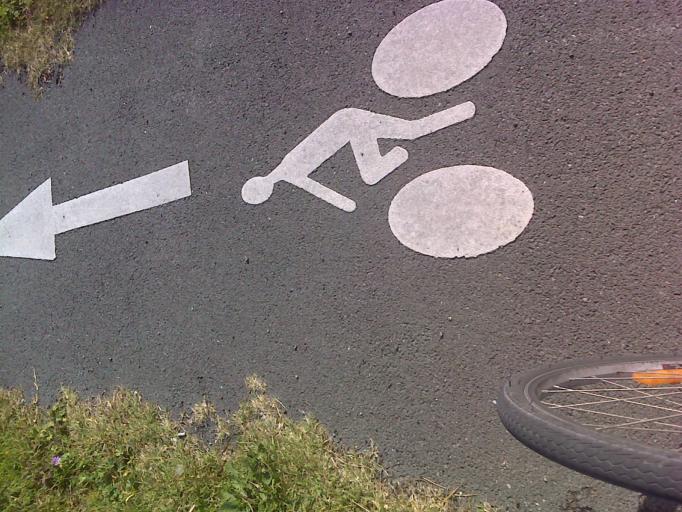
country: FR
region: Poitou-Charentes
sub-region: Departement de la Charente-Maritime
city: Marennes
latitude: 45.8300
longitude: -1.1199
